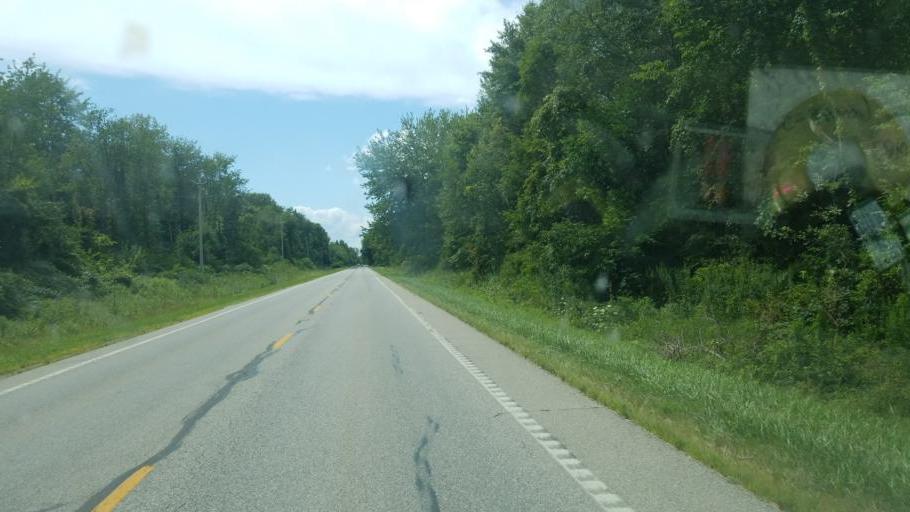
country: US
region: Ohio
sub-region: Delaware County
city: Sunbury
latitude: 40.2527
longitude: -82.8192
